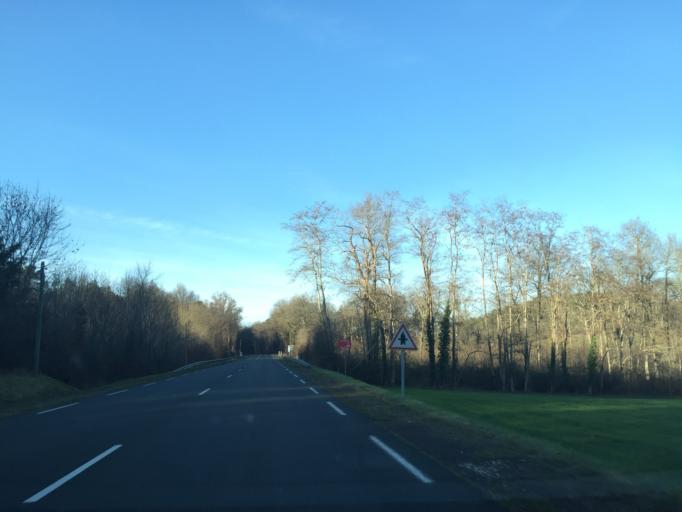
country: FR
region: Aquitaine
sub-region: Departement de la Dordogne
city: Riberac
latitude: 45.1785
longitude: 0.3861
